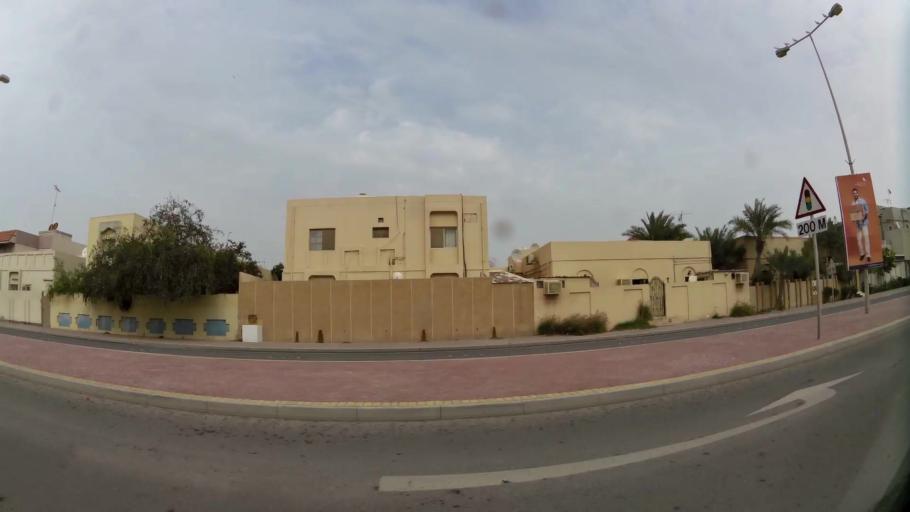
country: BH
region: Northern
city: Ar Rifa'
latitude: 26.1309
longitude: 50.5624
